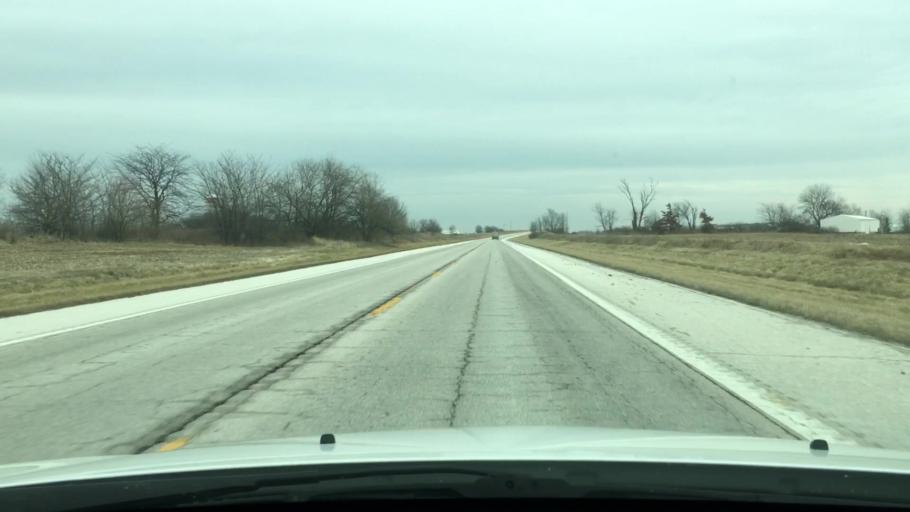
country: US
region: Missouri
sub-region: Pike County
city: Bowling Green
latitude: 39.3508
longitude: -91.2219
